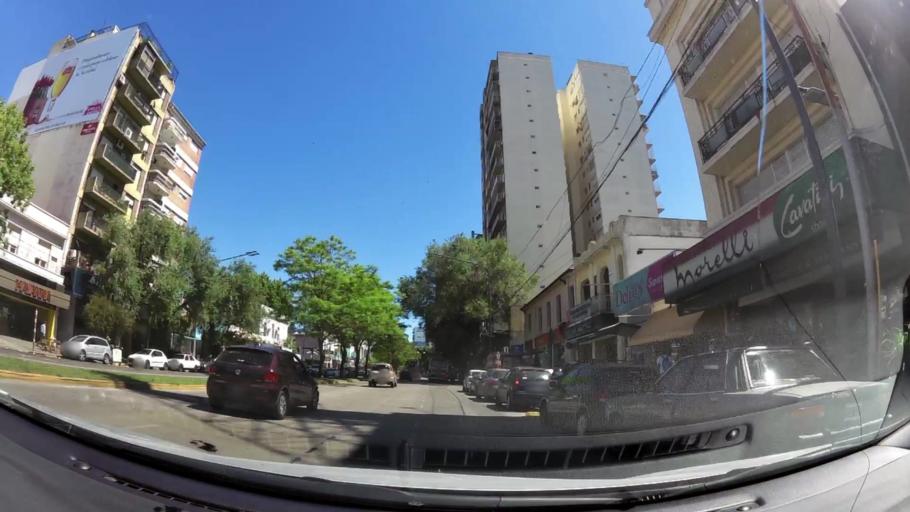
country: AR
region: Buenos Aires
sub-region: Partido de Vicente Lopez
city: Olivos
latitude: -34.5139
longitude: -58.4890
